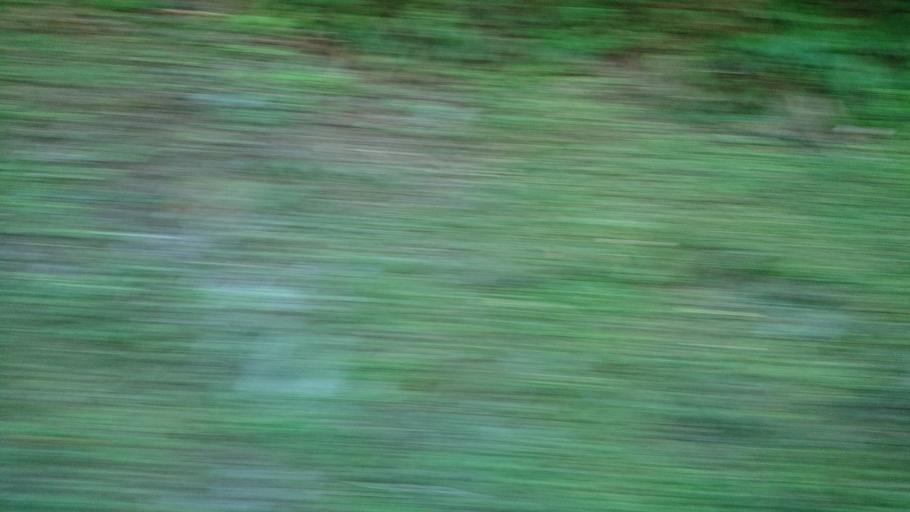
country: TW
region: Taiwan
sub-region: Yilan
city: Yilan
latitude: 24.5777
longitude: 121.4898
